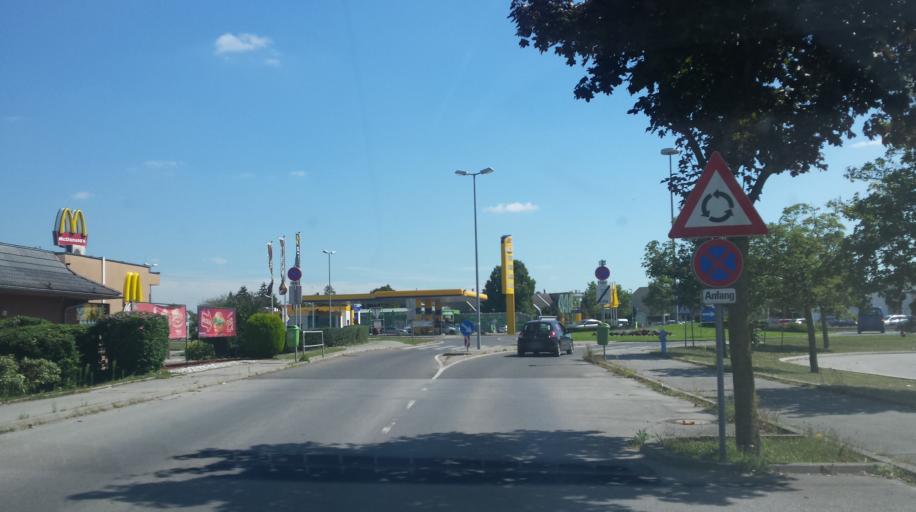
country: AT
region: Lower Austria
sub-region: Politischer Bezirk Ganserndorf
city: Deutsch-Wagram
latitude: 48.3034
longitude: 16.5761
